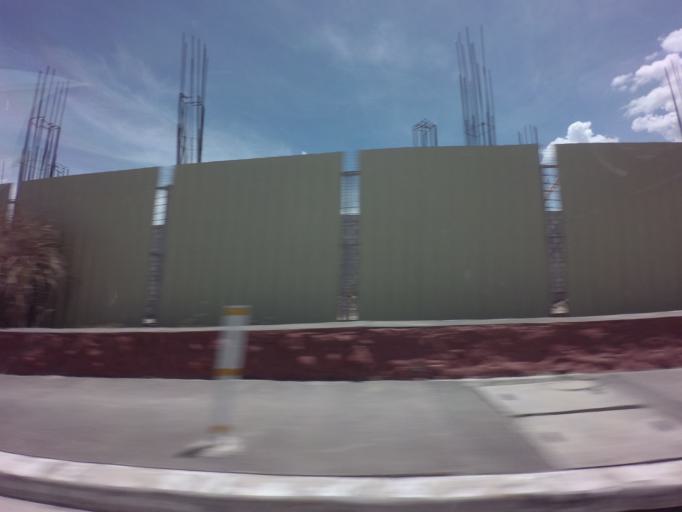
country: PH
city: Sambayanihan People's Village
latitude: 14.4887
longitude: 120.9995
